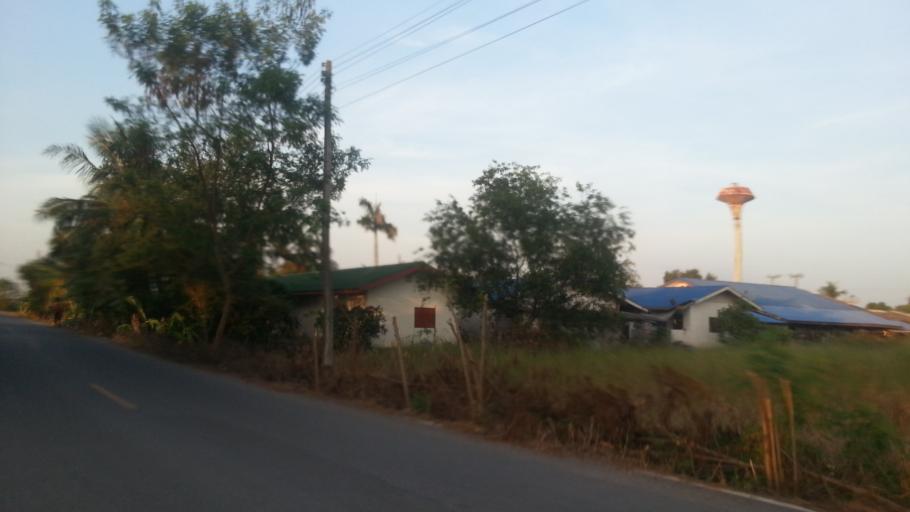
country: TH
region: Pathum Thani
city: Nong Suea
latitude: 14.0495
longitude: 100.8671
